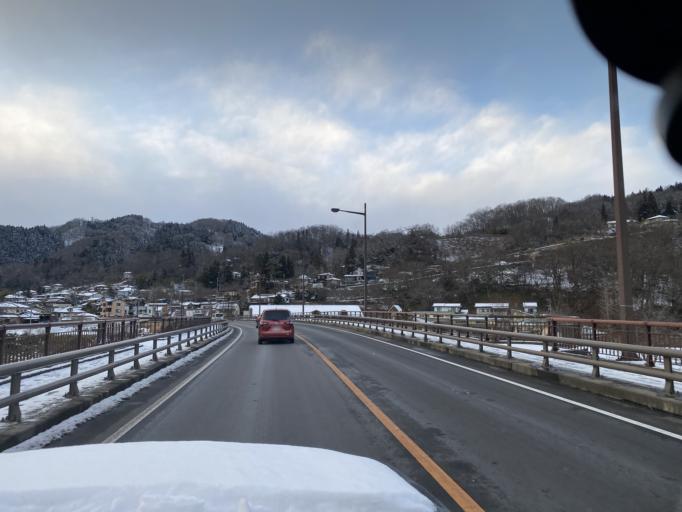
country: JP
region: Nagano
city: Nagano-shi
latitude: 36.6175
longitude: 138.0935
